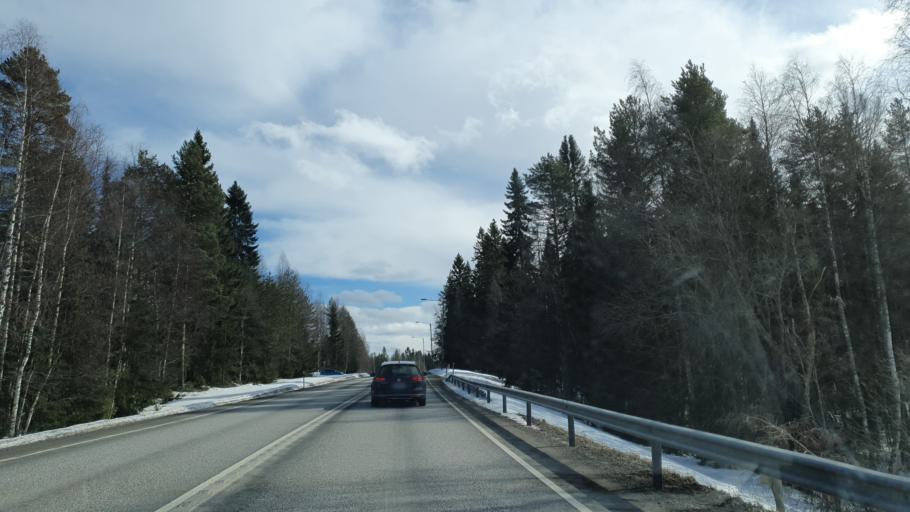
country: FI
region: Kainuu
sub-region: Kajaani
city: Paltamo
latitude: 64.3917
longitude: 27.9802
